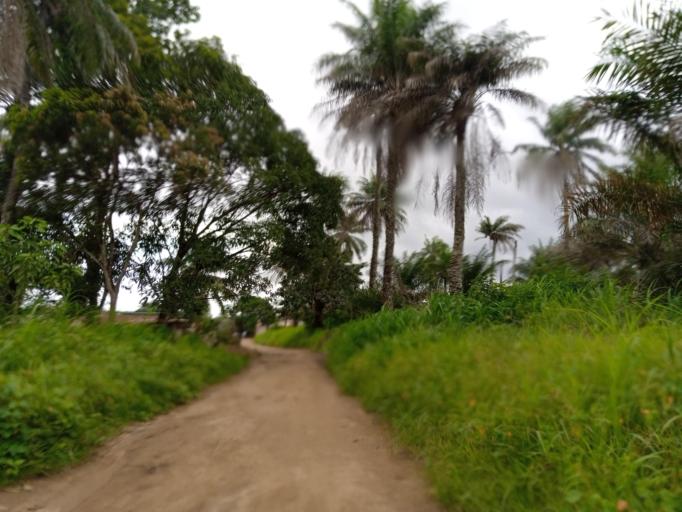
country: SL
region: Northern Province
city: Masoyila
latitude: 8.5781
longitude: -13.1629
